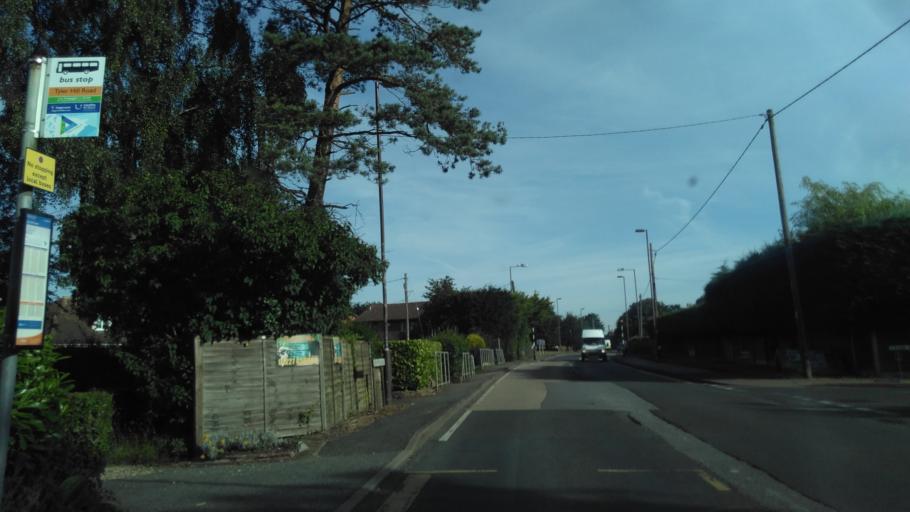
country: GB
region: England
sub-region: Kent
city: Blean
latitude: 51.3064
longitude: 1.0435
